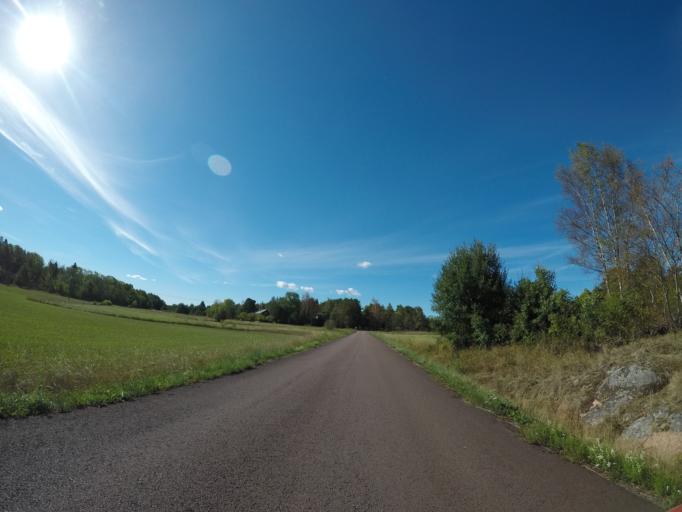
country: AX
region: Alands landsbygd
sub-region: Finstroem
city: Finstroem
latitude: 60.2975
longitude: 19.8799
